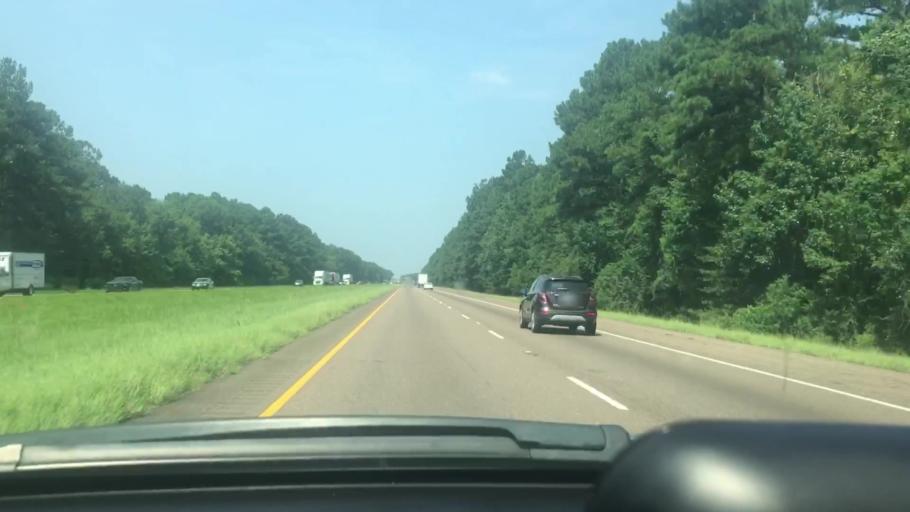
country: US
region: Louisiana
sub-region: Livingston Parish
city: Livingston
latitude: 30.4742
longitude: -90.7693
